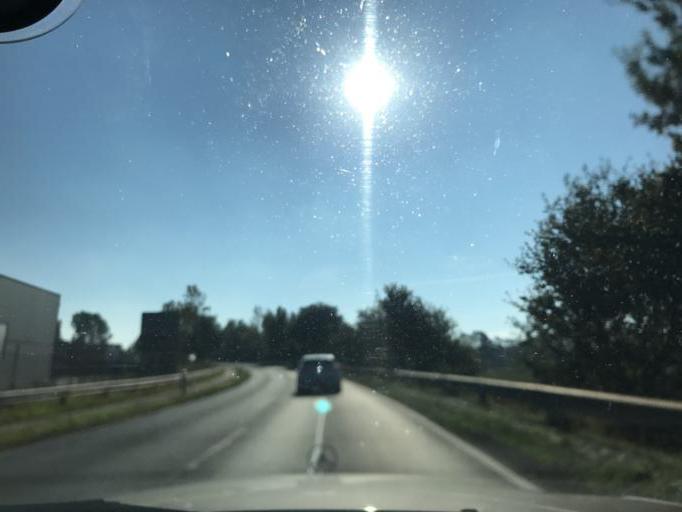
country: DE
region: Lower Saxony
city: Papenburg
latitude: 53.0859
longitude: 7.3739
